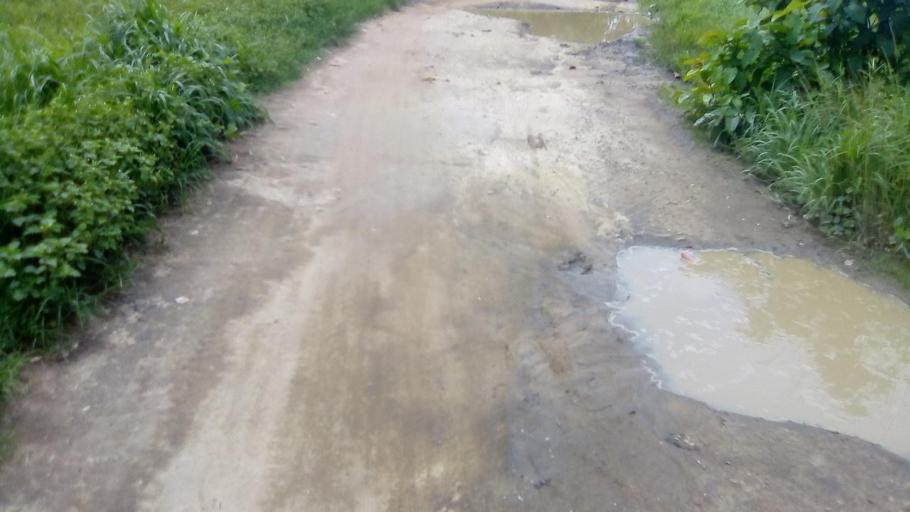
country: SL
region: Southern Province
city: Bo
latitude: 7.9380
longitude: -11.7458
